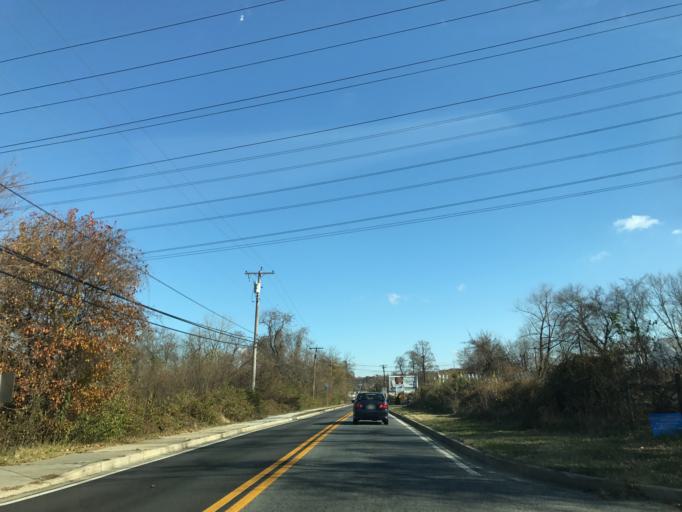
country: US
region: Maryland
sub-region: Anne Arundel County
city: Pumphrey
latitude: 39.2203
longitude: -76.6335
